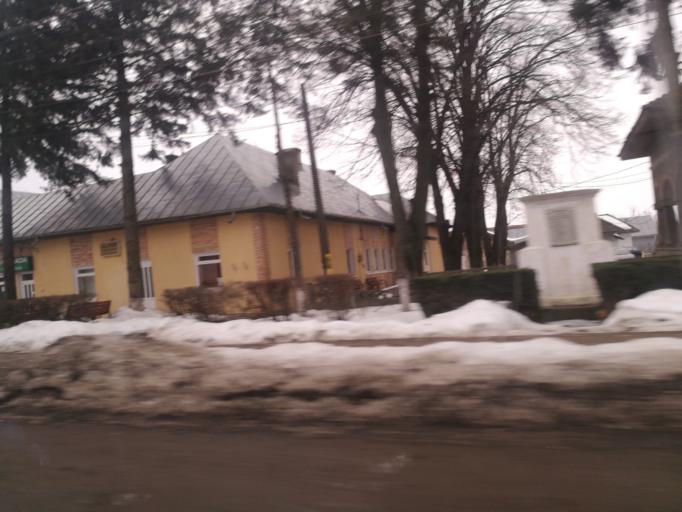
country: RO
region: Iasi
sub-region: Comuna Ruginoasa
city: Ruginoasa
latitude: 47.2423
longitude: 26.8417
